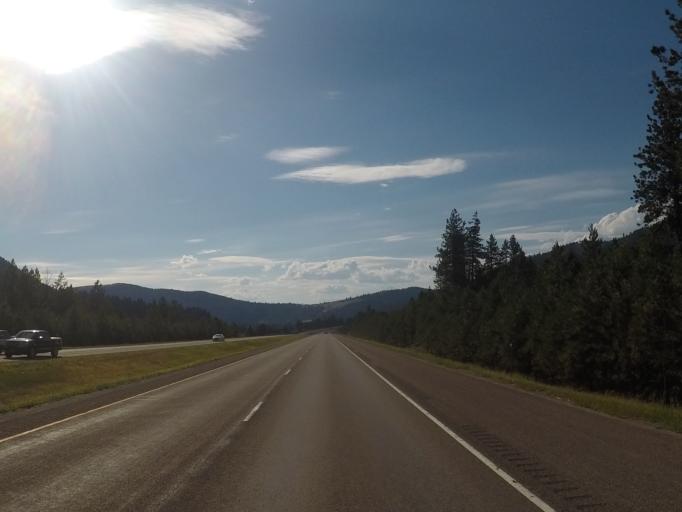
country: US
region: Montana
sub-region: Missoula County
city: Bonner-West Riverside
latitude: 46.8667
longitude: -113.8759
